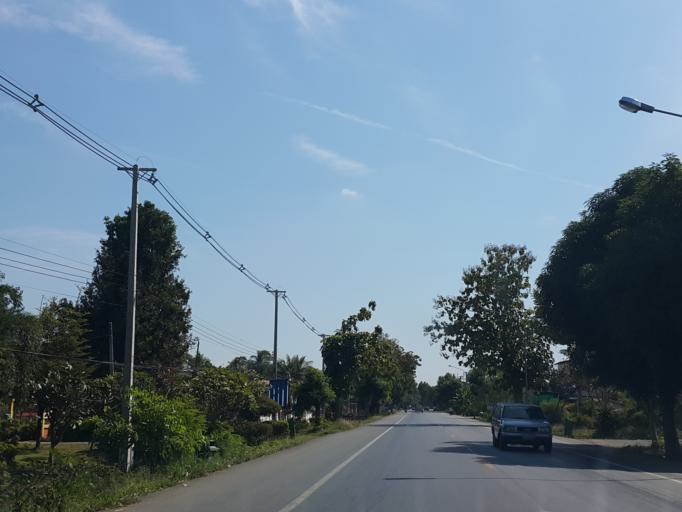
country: TH
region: Sukhothai
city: Sawankhalok
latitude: 17.2569
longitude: 99.8526
